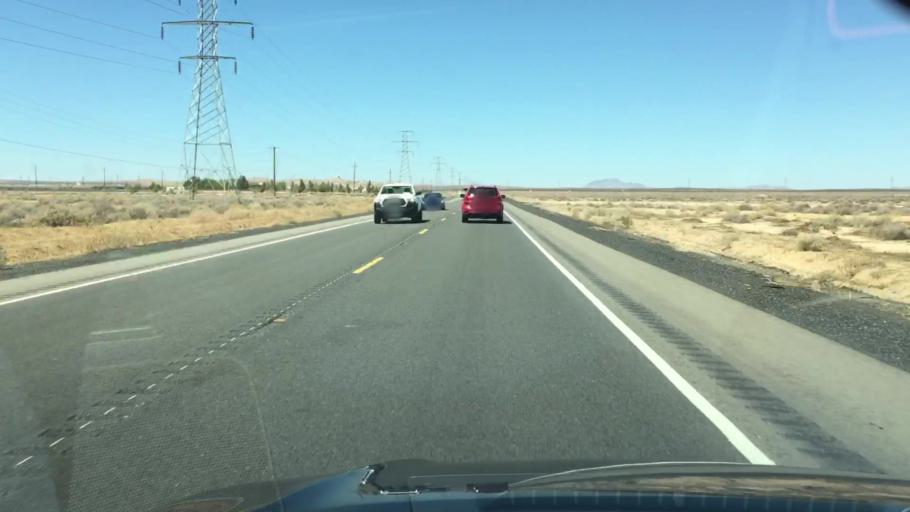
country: US
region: California
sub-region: Kern County
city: Boron
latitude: 35.0073
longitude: -117.5457
